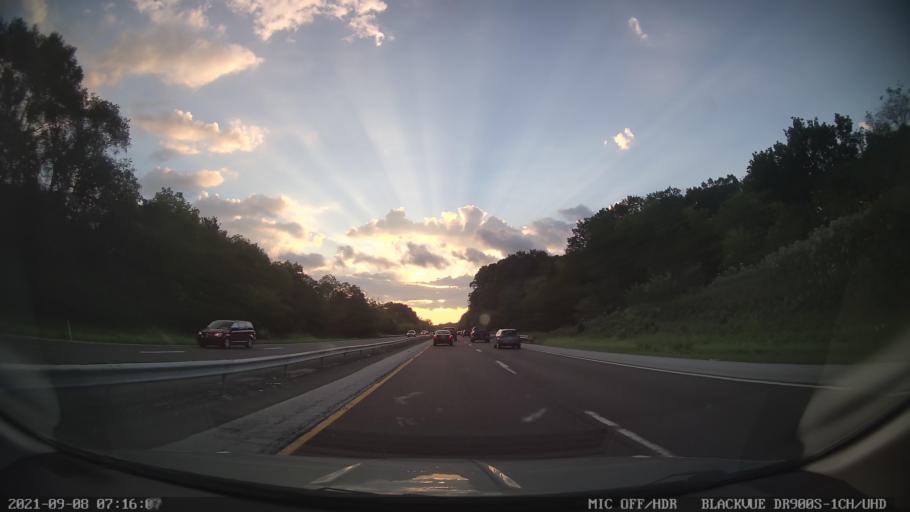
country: US
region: Pennsylvania
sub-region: Montgomery County
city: Sanatoga
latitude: 40.2407
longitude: -75.6048
